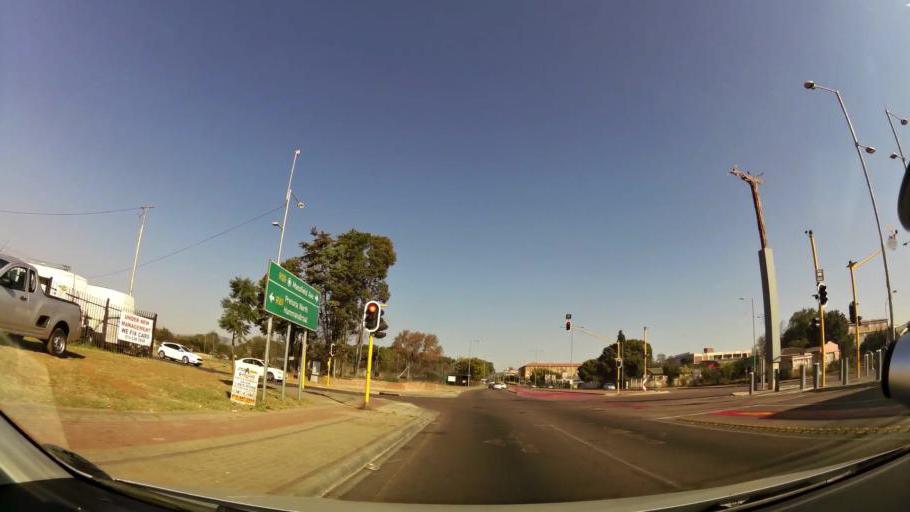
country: ZA
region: Gauteng
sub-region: City of Tshwane Metropolitan Municipality
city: Pretoria
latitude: -25.7076
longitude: 28.1869
